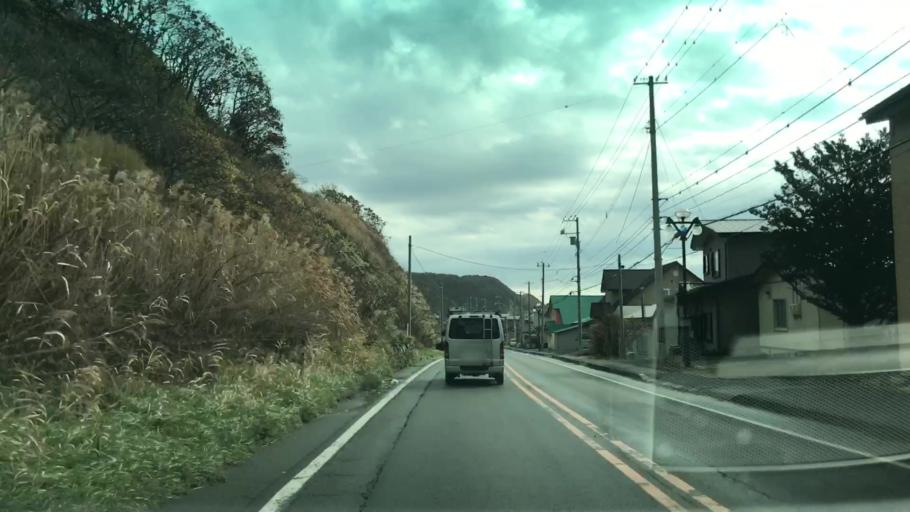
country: JP
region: Hokkaido
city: Shizunai-furukawacho
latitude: 42.1528
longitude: 142.7970
